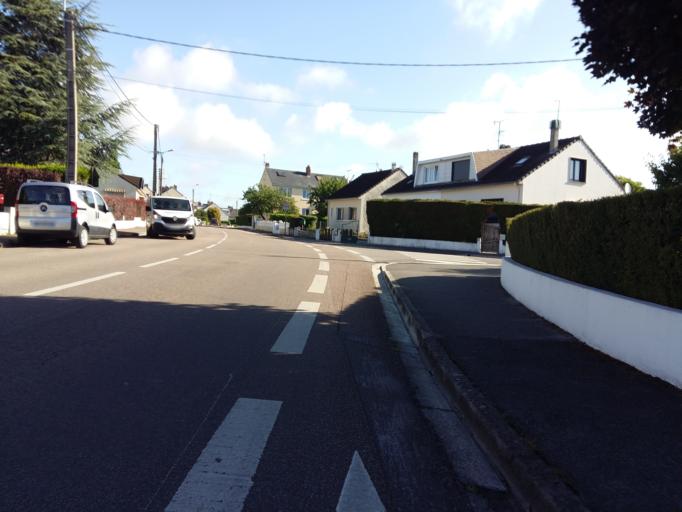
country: FR
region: Picardie
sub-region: Departement de la Somme
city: Rivery
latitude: 49.9064
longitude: 2.3265
